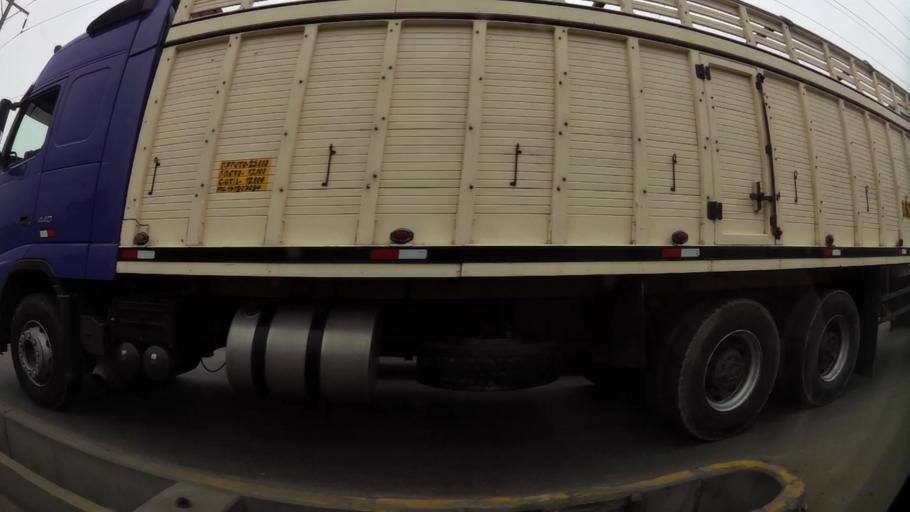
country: PE
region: Lima
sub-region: Lima
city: Punta Hermosa
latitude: -12.2788
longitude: -76.8683
